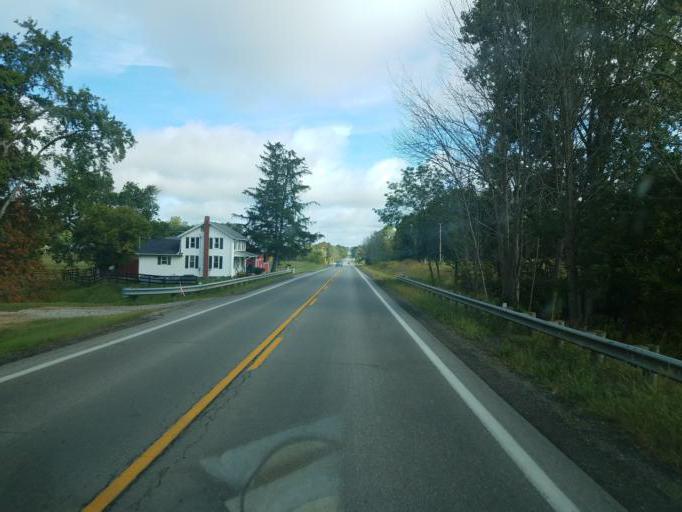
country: US
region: Ohio
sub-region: Wayne County
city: West Salem
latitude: 40.9436
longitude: -82.1094
